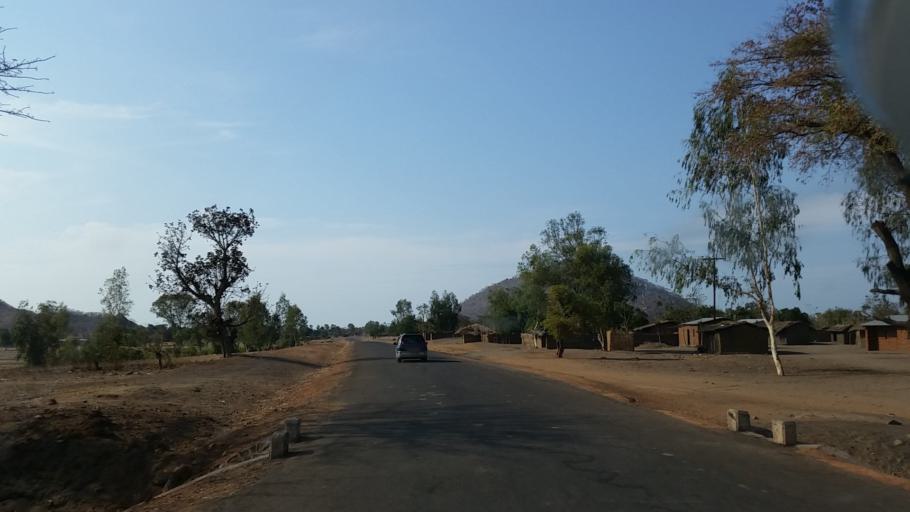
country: MW
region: Central Region
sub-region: Salima District
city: Salima
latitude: -13.6977
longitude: 34.5895
